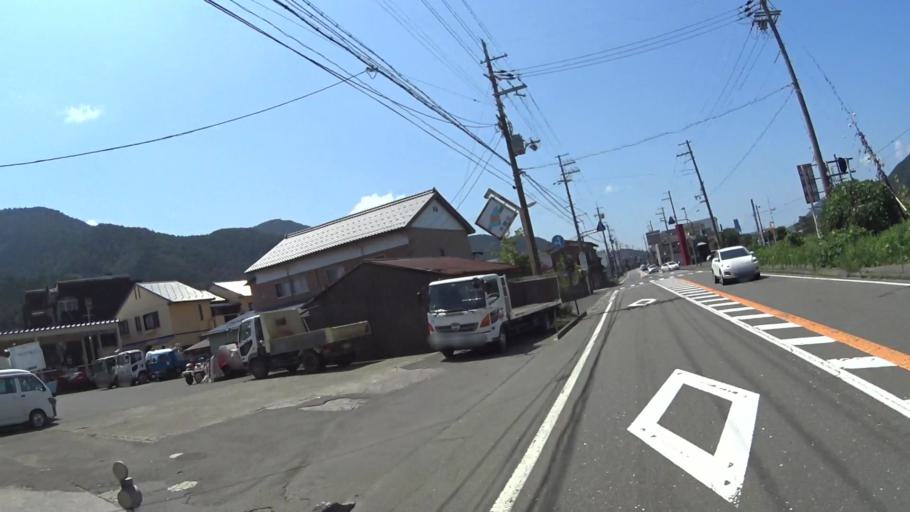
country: JP
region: Fukui
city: Obama
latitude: 35.4626
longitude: 135.8597
